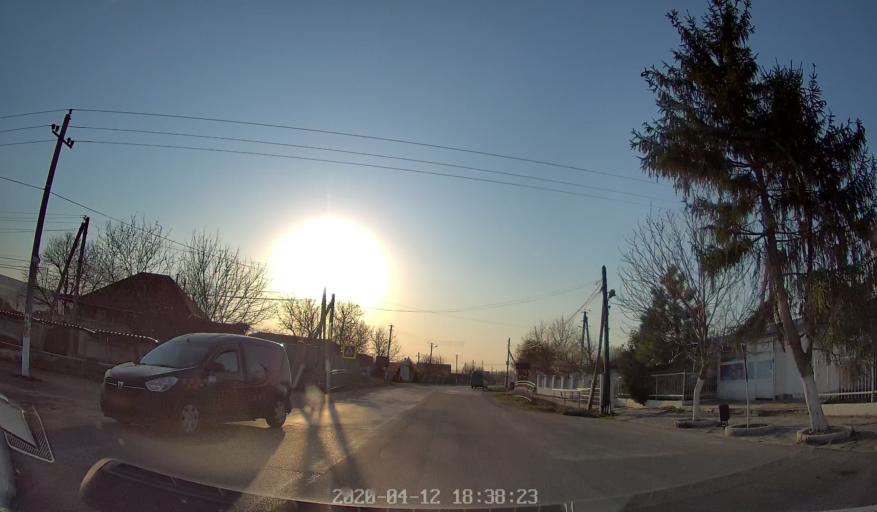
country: MD
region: Chisinau
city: Vadul lui Voda
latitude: 47.1241
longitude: 29.0015
